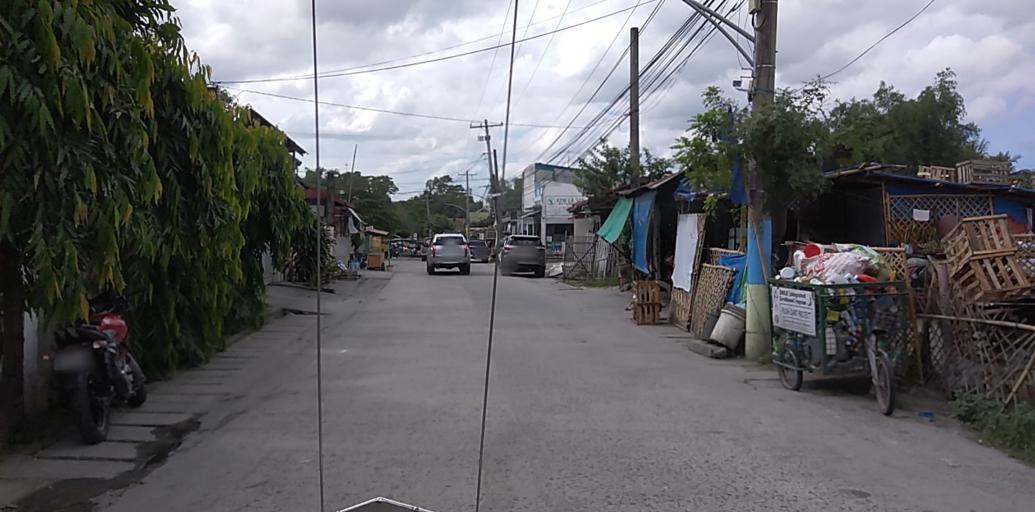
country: PH
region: Central Luzon
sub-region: Province of Pampanga
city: Porac
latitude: 15.0721
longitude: 120.5421
